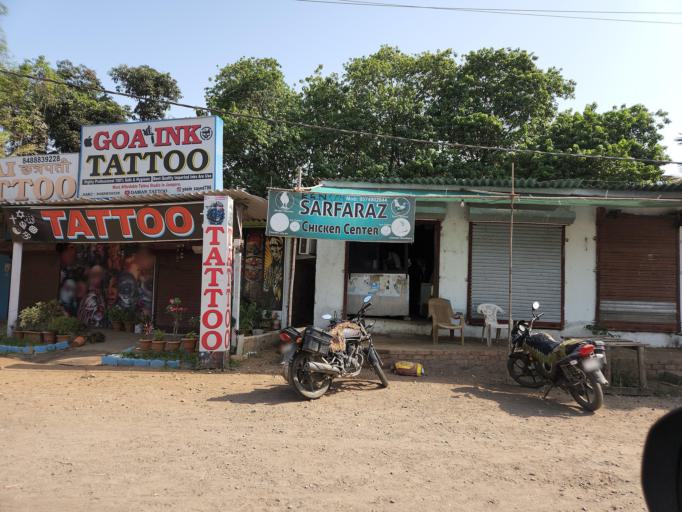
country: IN
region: Daman and Diu
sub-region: Daman District
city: Daman
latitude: 20.3769
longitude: 72.8249
